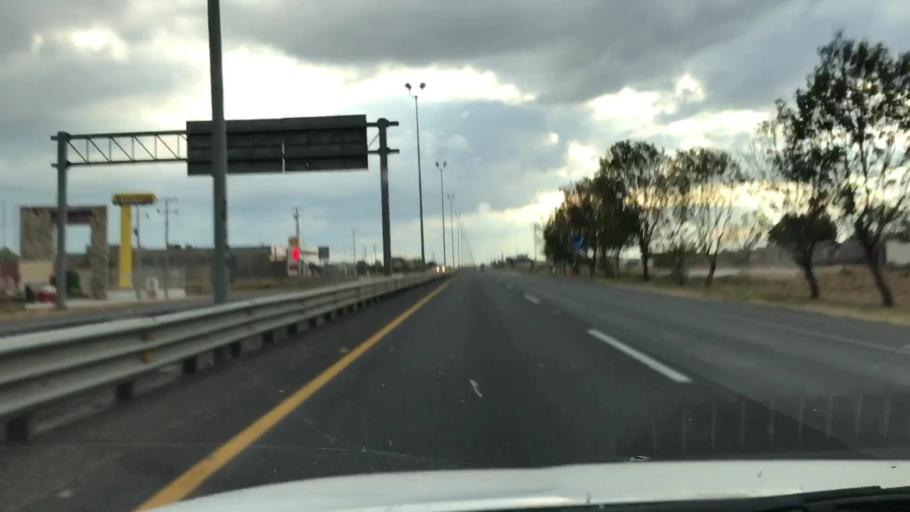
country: MX
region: Guanajuato
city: Penjamo
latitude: 20.4326
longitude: -101.7021
